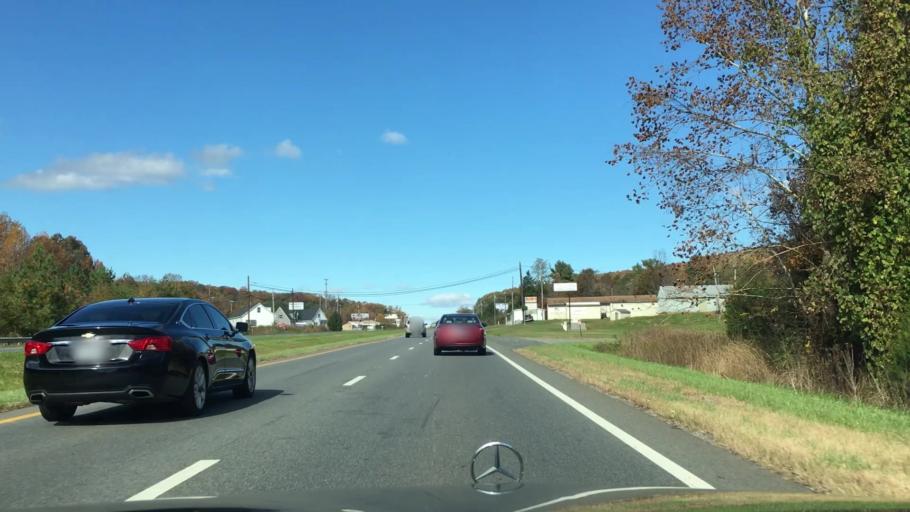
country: US
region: Virginia
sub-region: Campbell County
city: Rustburg
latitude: 37.2911
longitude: -79.1690
